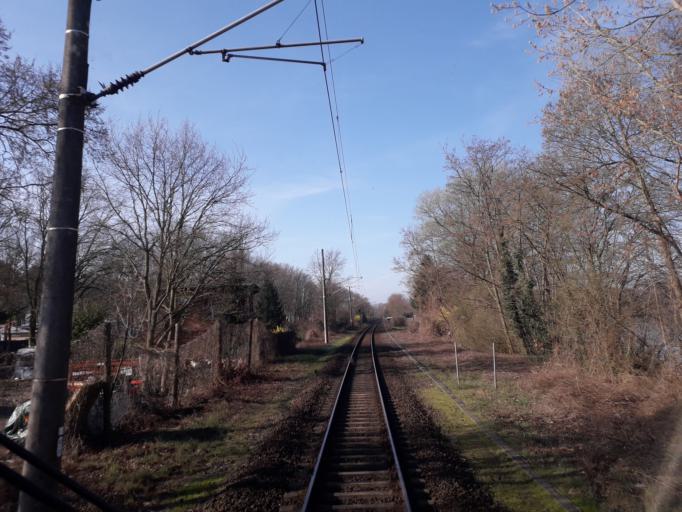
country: DE
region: Brandenburg
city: Michendorf
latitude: 52.3550
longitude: 12.9918
